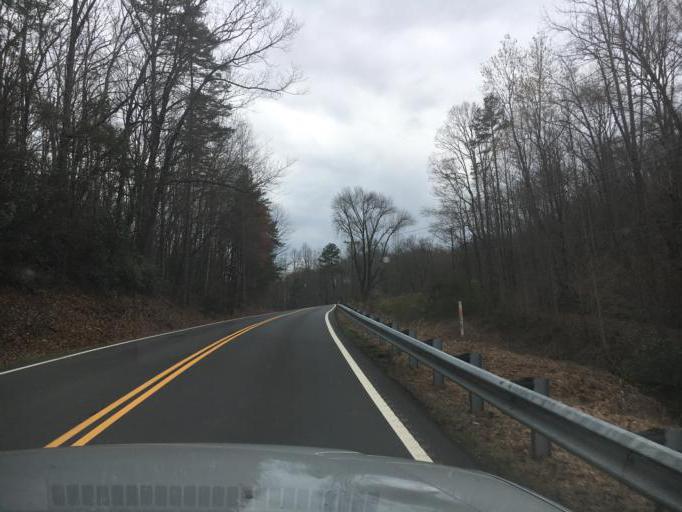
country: US
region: South Carolina
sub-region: Pickens County
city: Pickens
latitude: 34.9833
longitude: -82.7545
